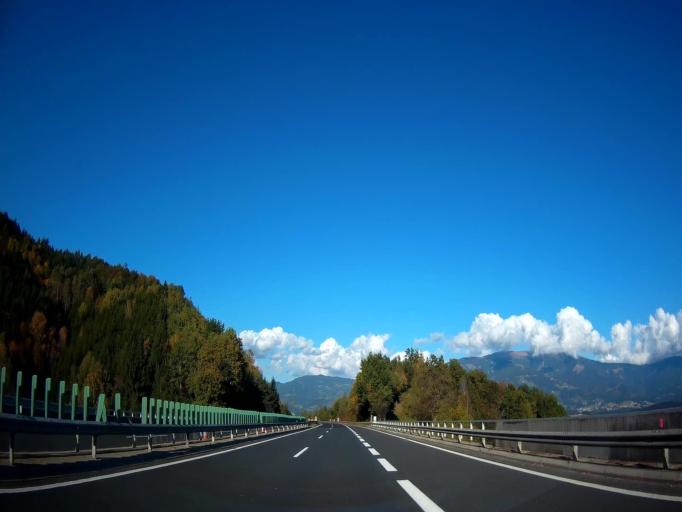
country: AT
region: Carinthia
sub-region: Politischer Bezirk Wolfsberg
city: Sankt Andrae
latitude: 46.7469
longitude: 14.8114
